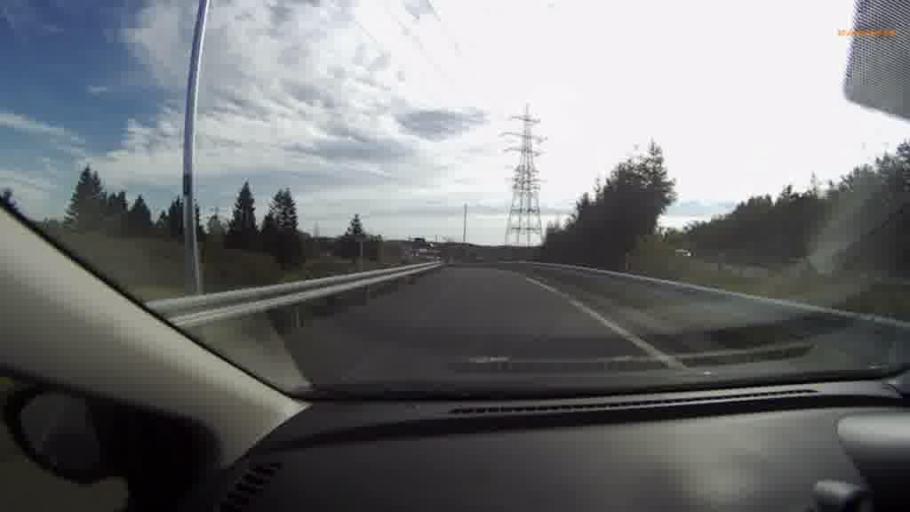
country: JP
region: Hokkaido
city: Kushiro
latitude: 43.0230
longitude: 144.4154
